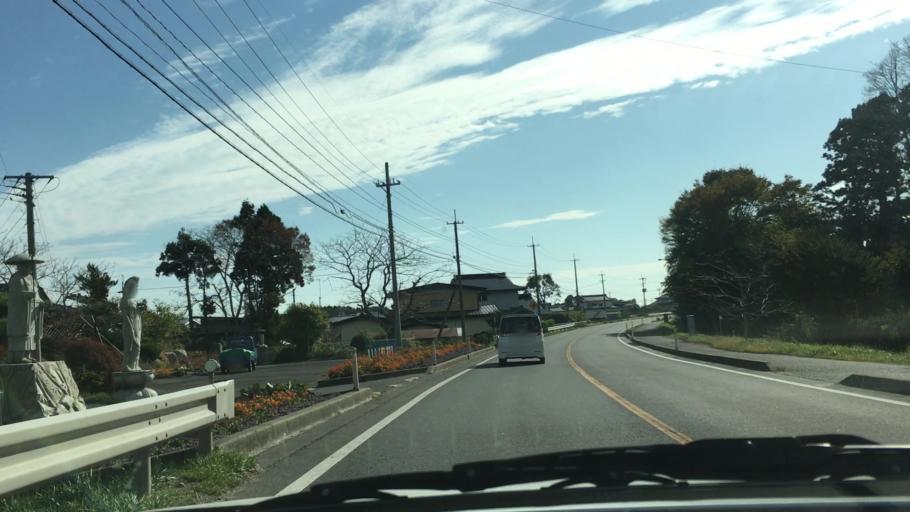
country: JP
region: Aomori
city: Hachinohe
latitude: 40.4259
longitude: 141.6961
